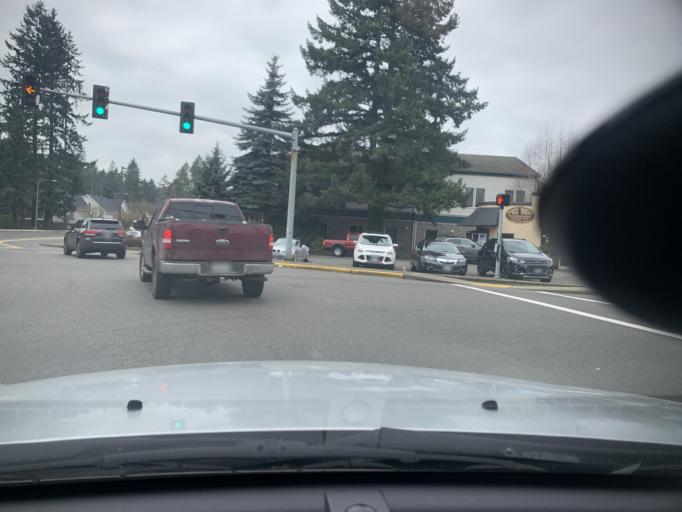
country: US
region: Washington
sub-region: Pierce County
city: Fircrest
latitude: 47.2392
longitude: -122.5160
